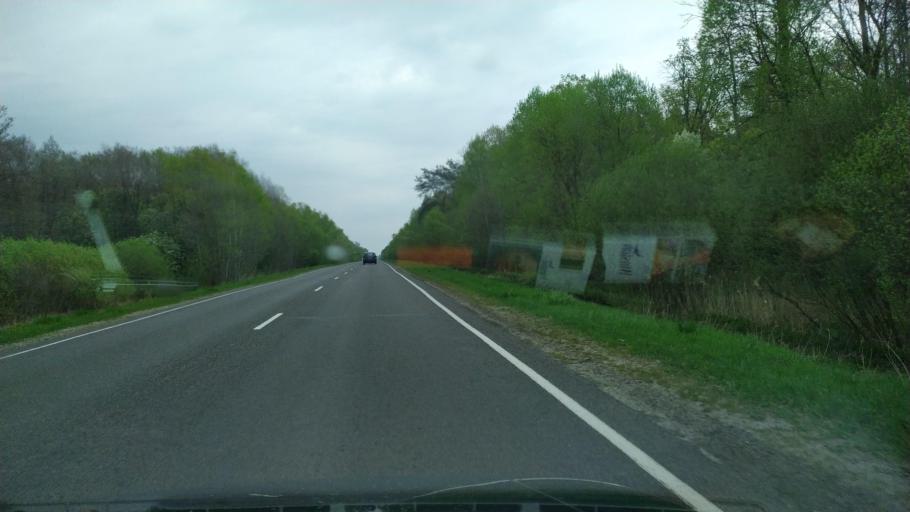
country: BY
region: Brest
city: Horad Kobryn
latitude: 52.3056
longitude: 24.5299
